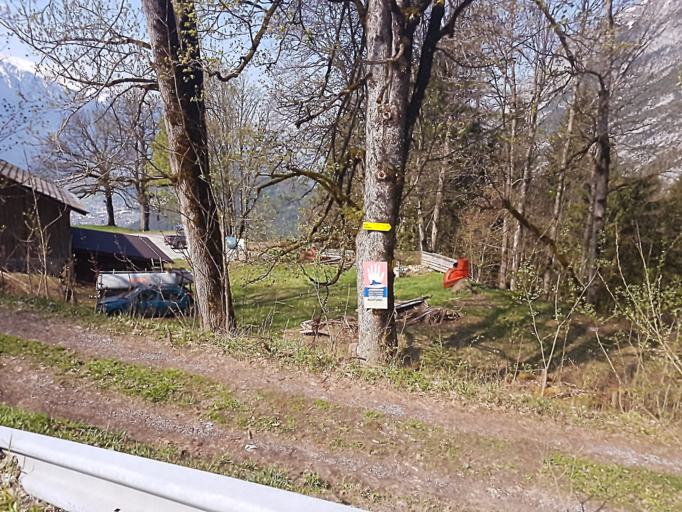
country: AT
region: Tyrol
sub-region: Politischer Bezirk Innsbruck Land
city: Pfaffenhofen
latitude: 47.3353
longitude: 11.1068
